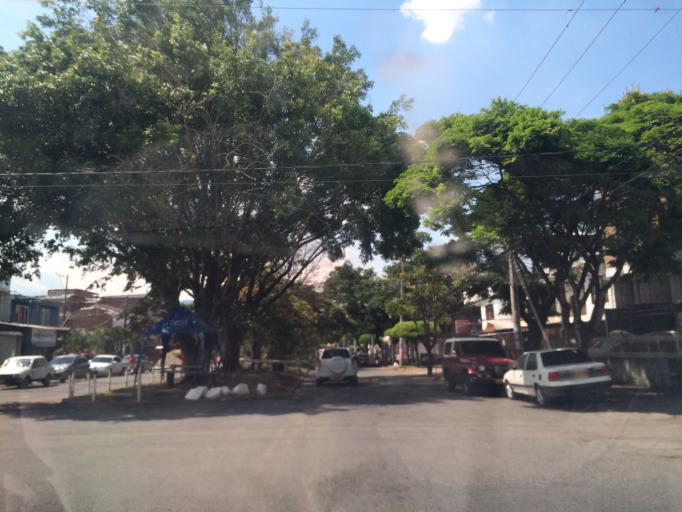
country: CO
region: Valle del Cauca
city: Cali
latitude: 3.4160
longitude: -76.5244
